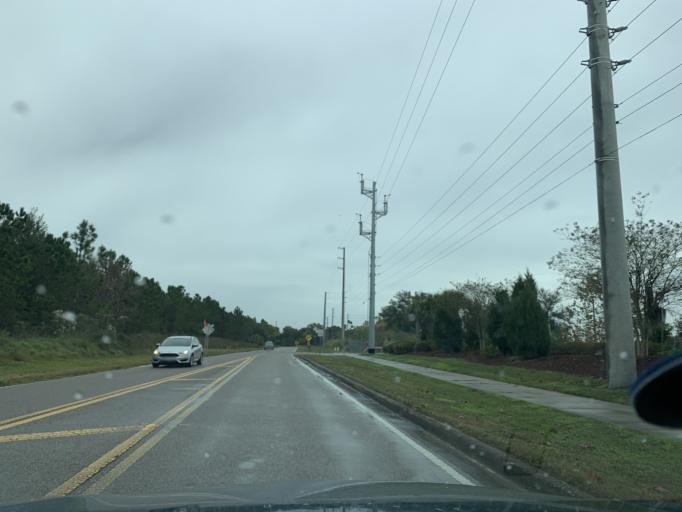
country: US
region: Florida
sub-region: Pasco County
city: Wesley Chapel
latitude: 28.2744
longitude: -82.3202
